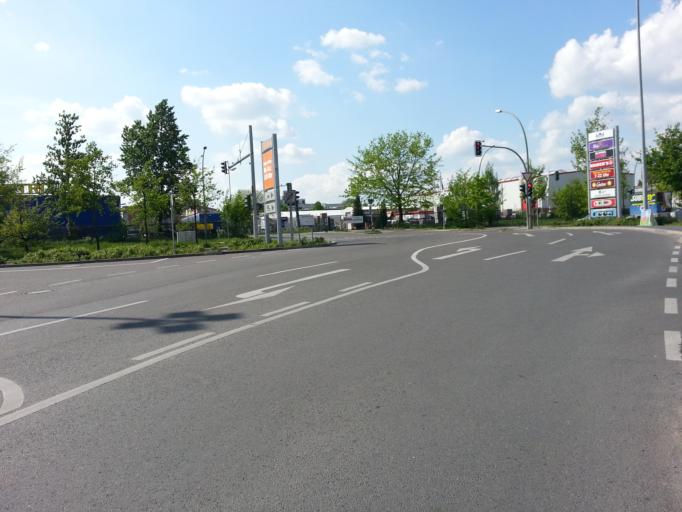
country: DE
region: Berlin
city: Haselhorst
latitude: 52.5399
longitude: 13.2485
